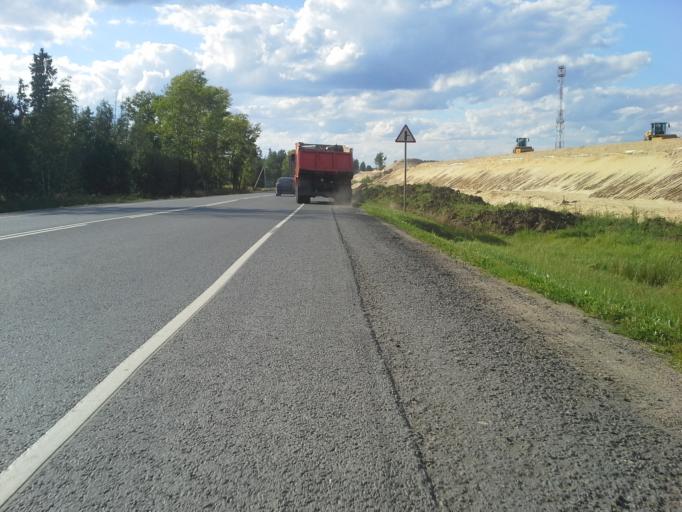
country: RU
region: Moskovskaya
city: Klimovsk
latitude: 55.3587
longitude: 37.4359
